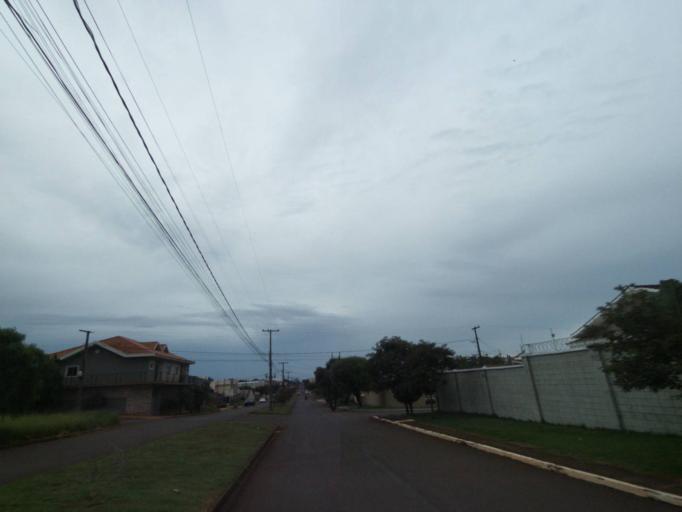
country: BR
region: Parana
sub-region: Campo Mourao
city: Campo Mourao
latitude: -24.0320
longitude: -52.3601
